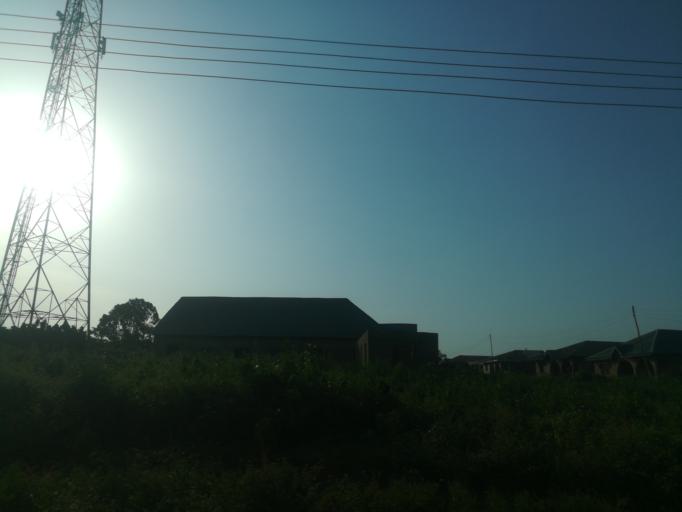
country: NG
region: Oyo
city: Moniya
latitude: 7.5651
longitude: 3.8859
